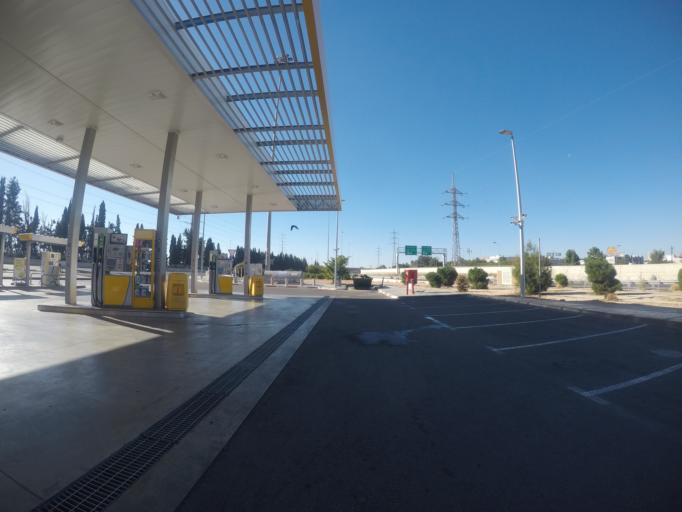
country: IL
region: Central District
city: Bet Dagan
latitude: 32.0025
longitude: 34.8076
